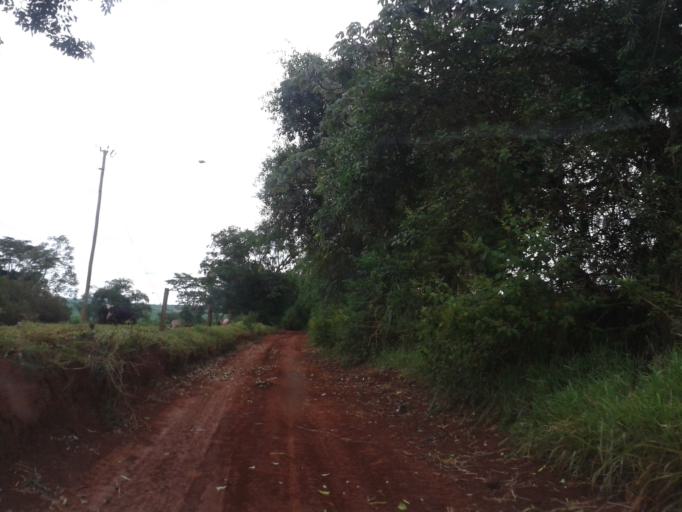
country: BR
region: Minas Gerais
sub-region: Centralina
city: Centralina
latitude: -18.6515
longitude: -49.3393
